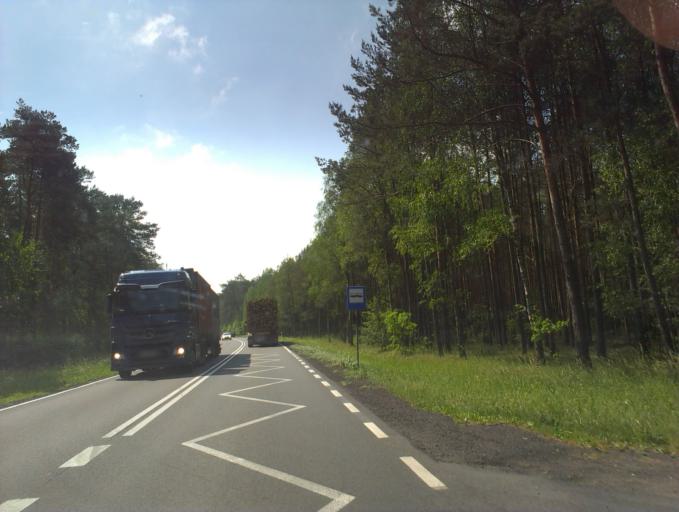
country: PL
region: Greater Poland Voivodeship
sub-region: Powiat zlotowski
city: Tarnowka
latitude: 53.3462
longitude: 16.7896
